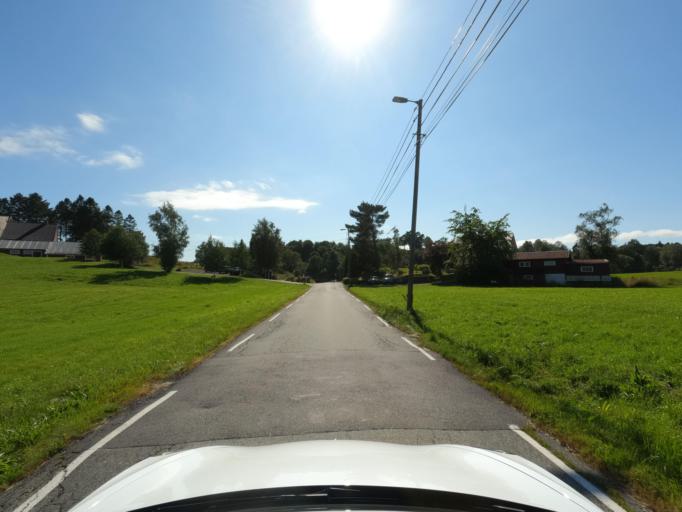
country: NO
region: Hordaland
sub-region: Bergen
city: Sandsli
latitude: 60.2667
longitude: 5.3143
